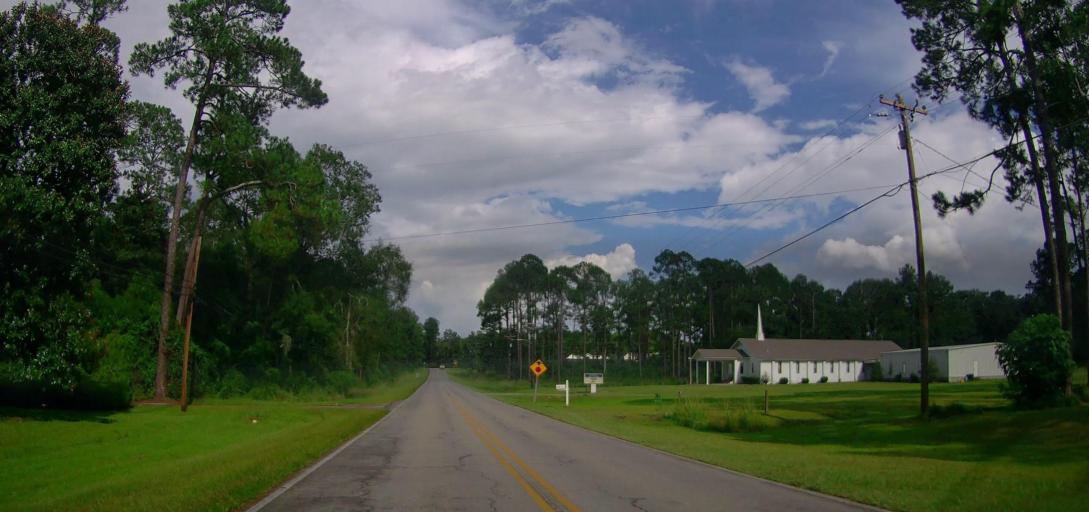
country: US
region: Georgia
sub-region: Coffee County
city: Douglas
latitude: 31.5154
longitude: -82.8308
